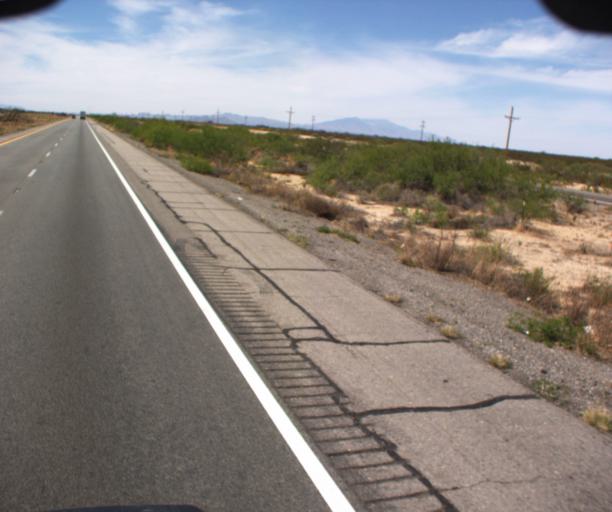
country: US
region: Arizona
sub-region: Cochise County
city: Willcox
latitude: 32.2983
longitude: -109.3575
